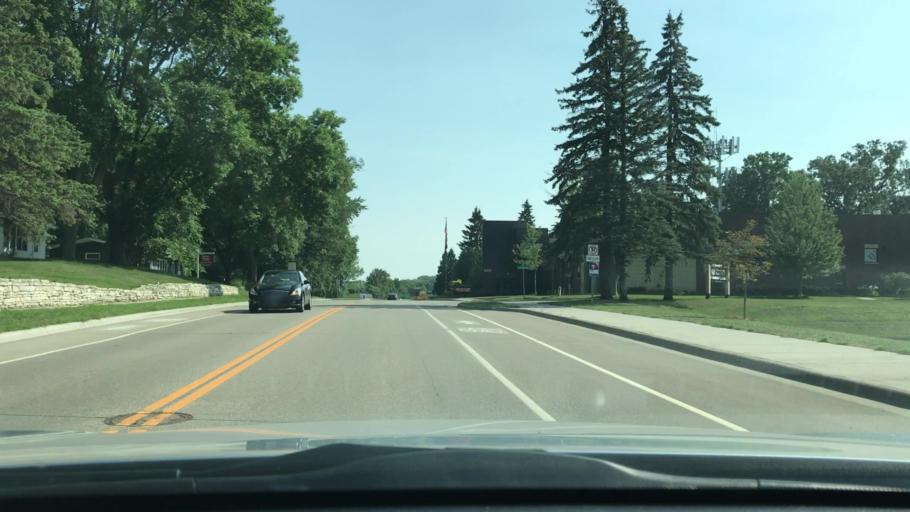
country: US
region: Minnesota
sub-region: Hennepin County
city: Edina
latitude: 44.8901
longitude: -93.3689
